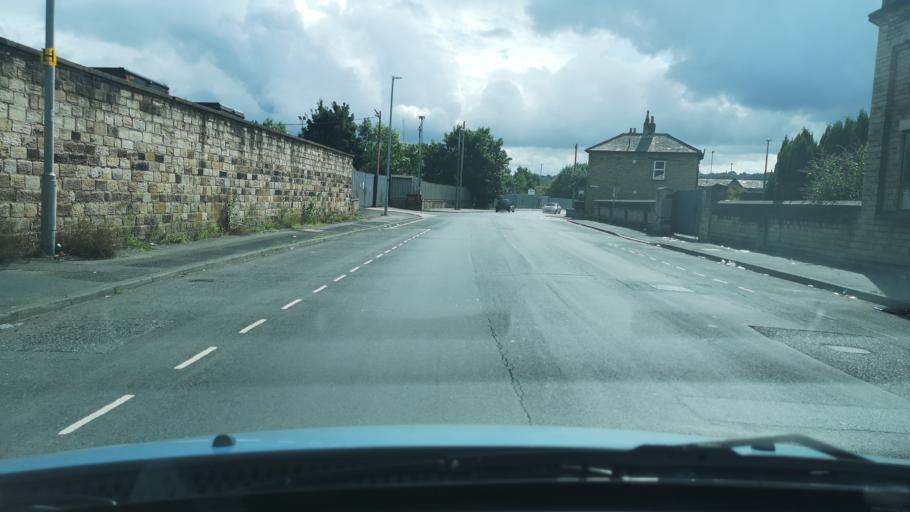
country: GB
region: England
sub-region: Kirklees
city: Dewsbury
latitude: 53.6850
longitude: -1.6232
